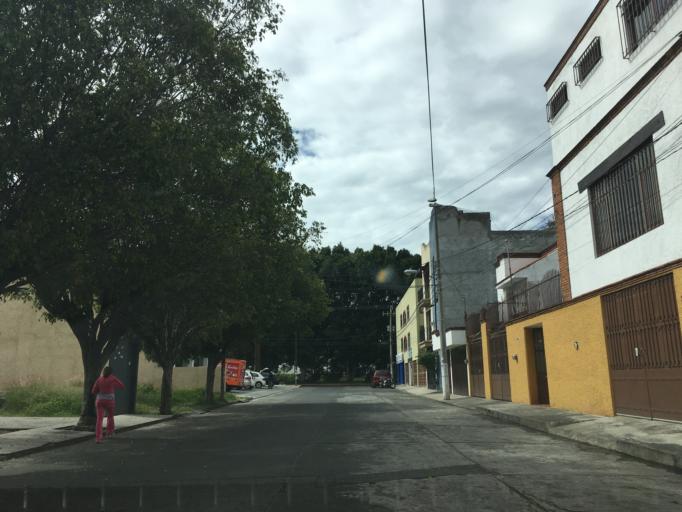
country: MX
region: Michoacan
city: Morelia
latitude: 19.6884
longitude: -101.1778
